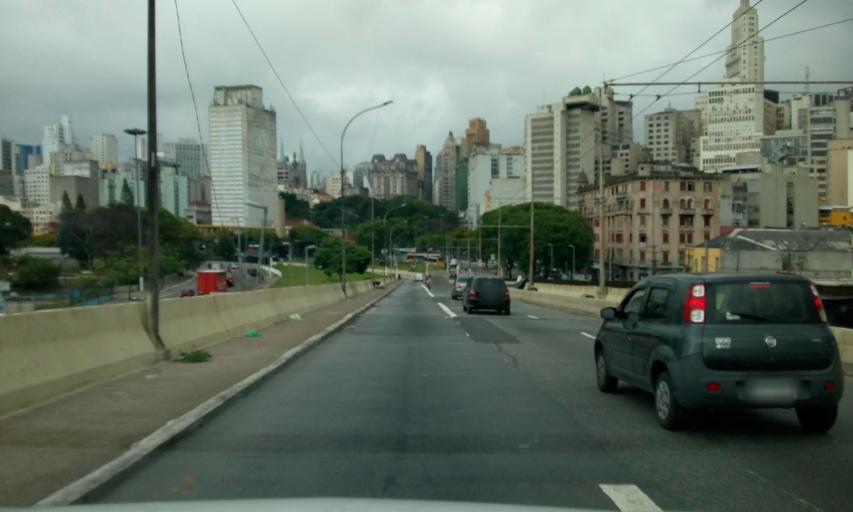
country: BR
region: Sao Paulo
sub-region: Sao Paulo
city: Sao Paulo
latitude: -23.5437
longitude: -46.6294
